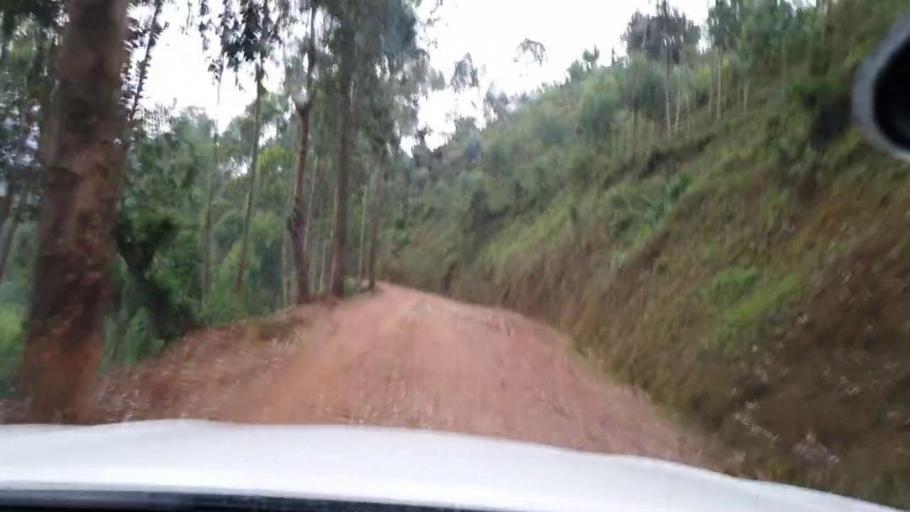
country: RW
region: Western Province
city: Cyangugu
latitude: -2.4085
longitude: 29.2058
